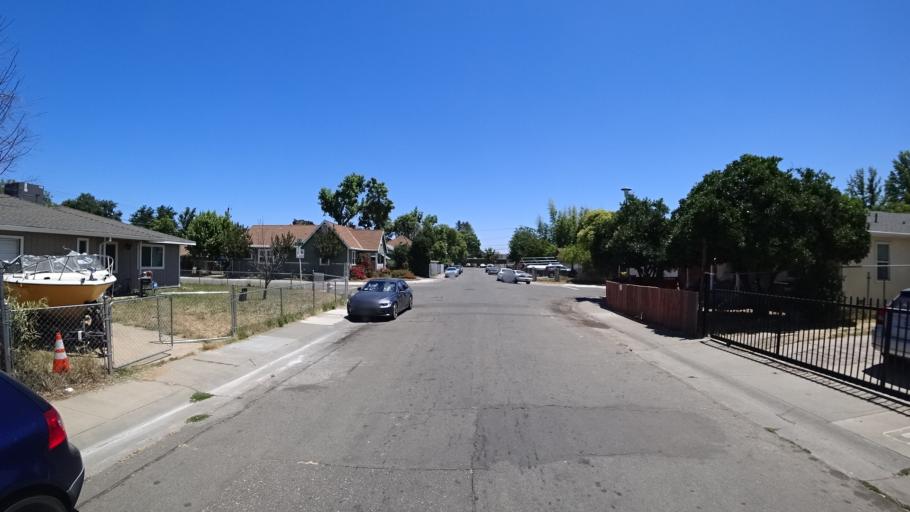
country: US
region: California
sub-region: Sacramento County
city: Parkway
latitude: 38.5354
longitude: -121.4661
